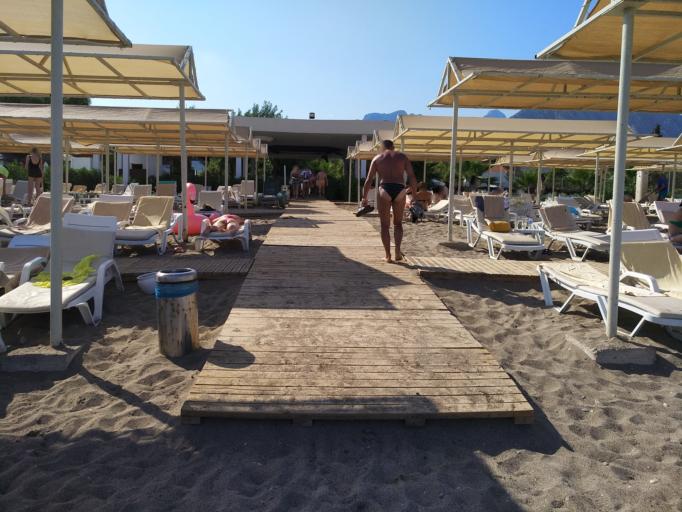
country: TR
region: Antalya
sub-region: Kemer
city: Goeynuek
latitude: 36.6653
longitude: 30.5636
